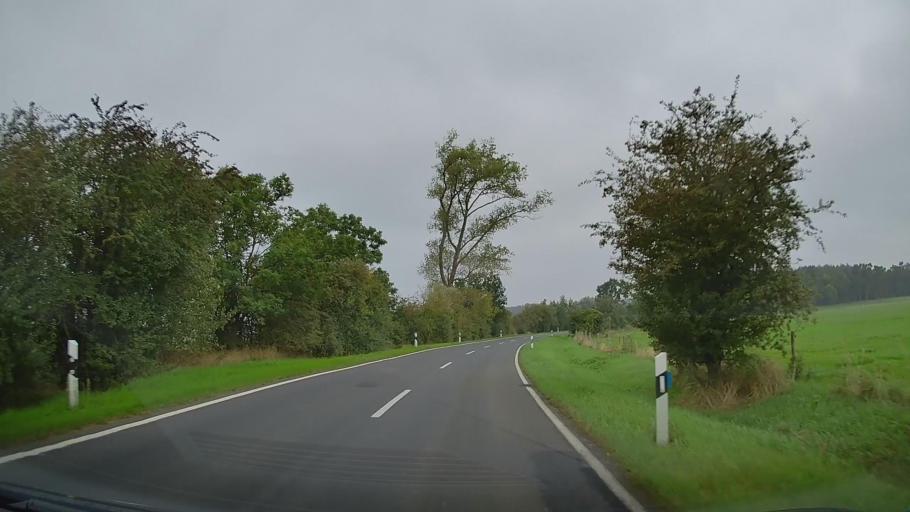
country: DE
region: Mecklenburg-Vorpommern
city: Neubukow
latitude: 54.0781
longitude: 11.6317
